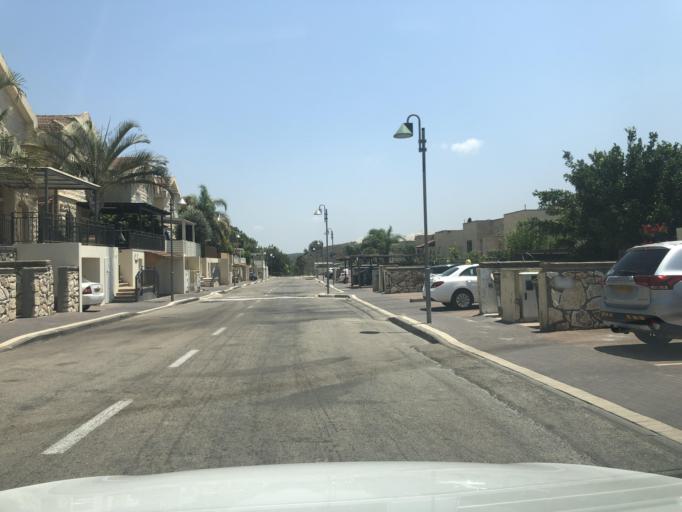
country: IL
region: Haifa
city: Daliyat el Karmil
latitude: 32.6358
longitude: 35.0857
